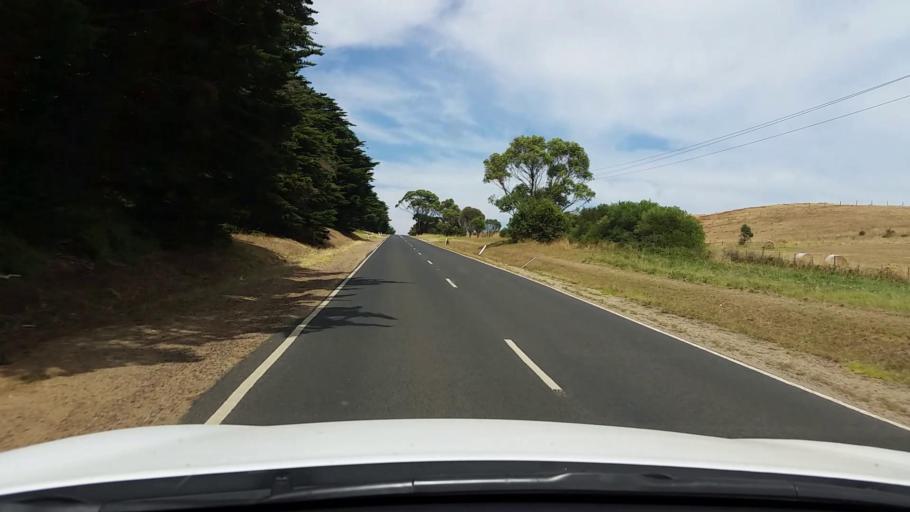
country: AU
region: Victoria
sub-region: Mornington Peninsula
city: Merricks
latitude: -38.4749
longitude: 144.9966
